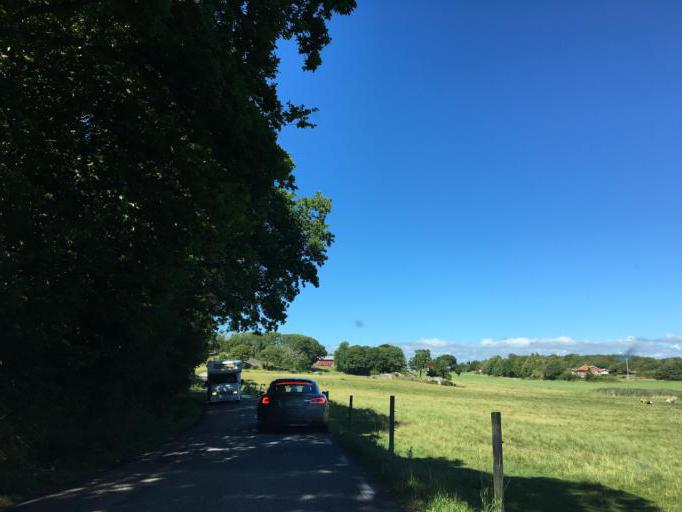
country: SE
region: Vaestra Goetaland
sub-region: Sotenas Kommun
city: Hunnebostrand
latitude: 58.4236
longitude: 11.2660
